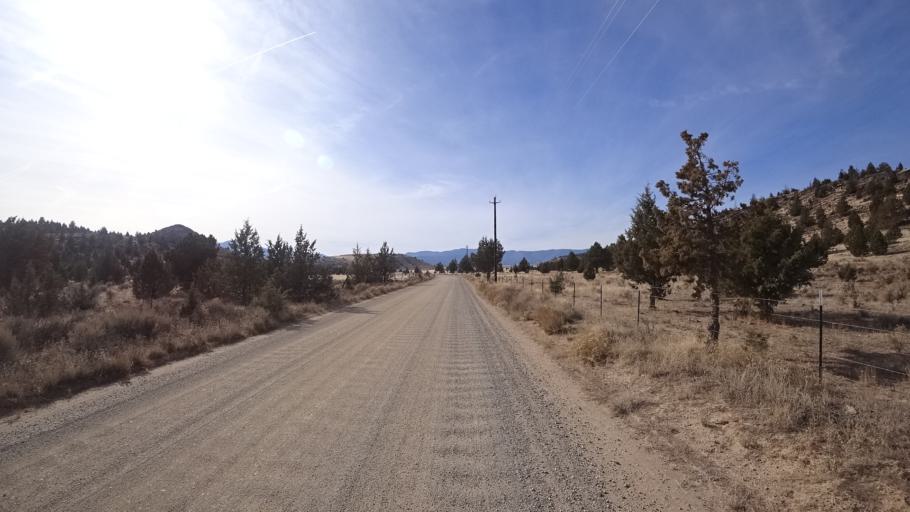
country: US
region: California
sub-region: Siskiyou County
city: Montague
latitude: 41.5792
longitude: -122.4591
